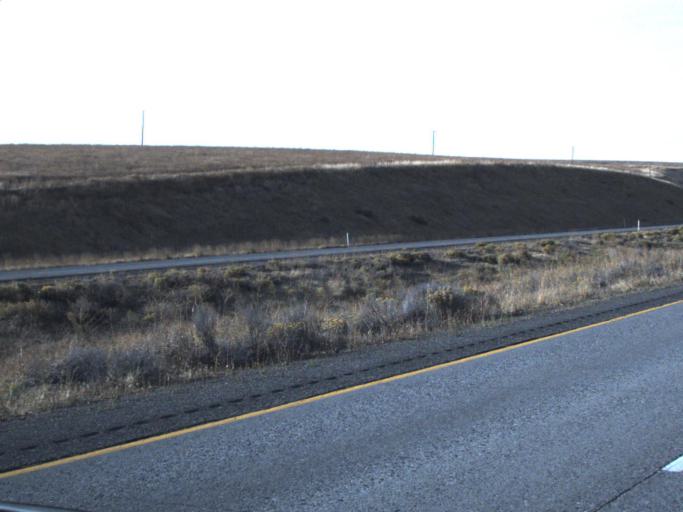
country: US
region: Washington
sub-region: Benton County
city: Highland
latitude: 46.0801
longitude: -119.2218
